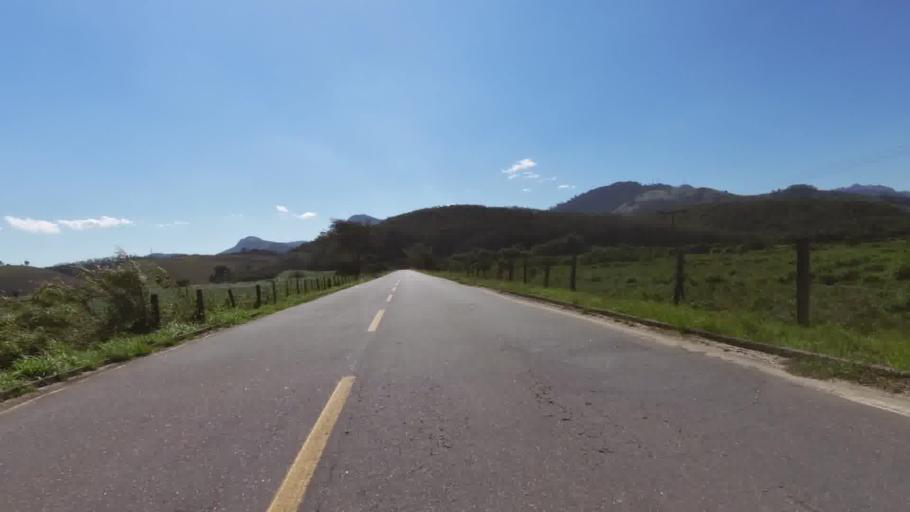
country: BR
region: Espirito Santo
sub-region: Rio Novo Do Sul
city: Rio Novo do Sul
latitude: -20.8857
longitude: -40.9028
